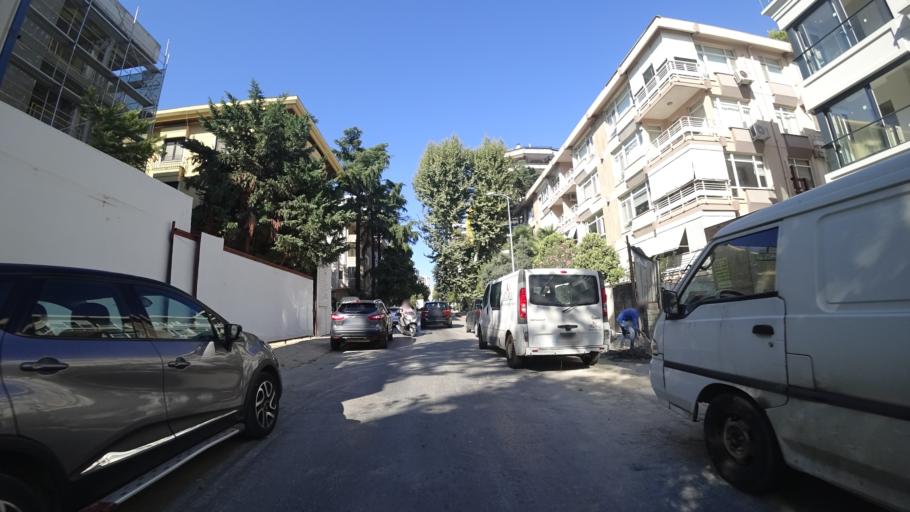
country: TR
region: Istanbul
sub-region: Atasehir
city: Atasehir
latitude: 40.9601
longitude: 29.0739
